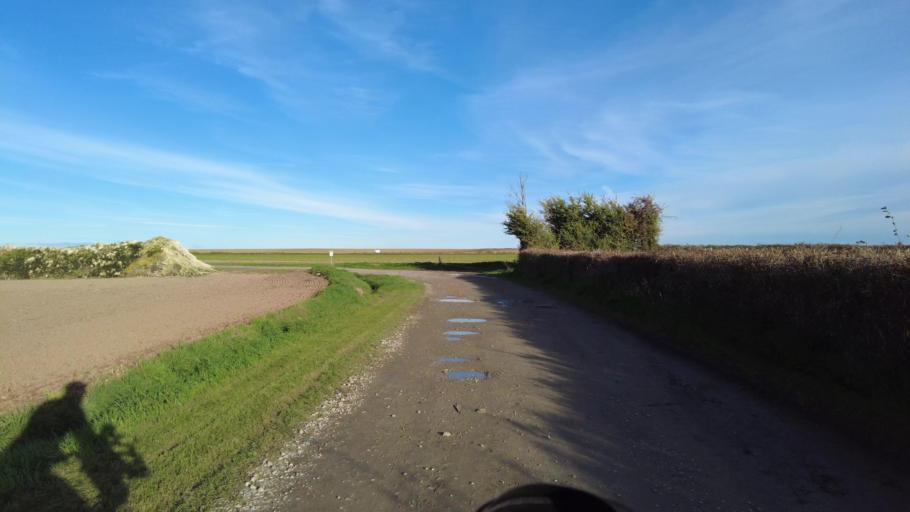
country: BE
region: Wallonia
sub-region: Province du Brabant Wallon
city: Jodoigne
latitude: 50.7090
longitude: 4.8999
